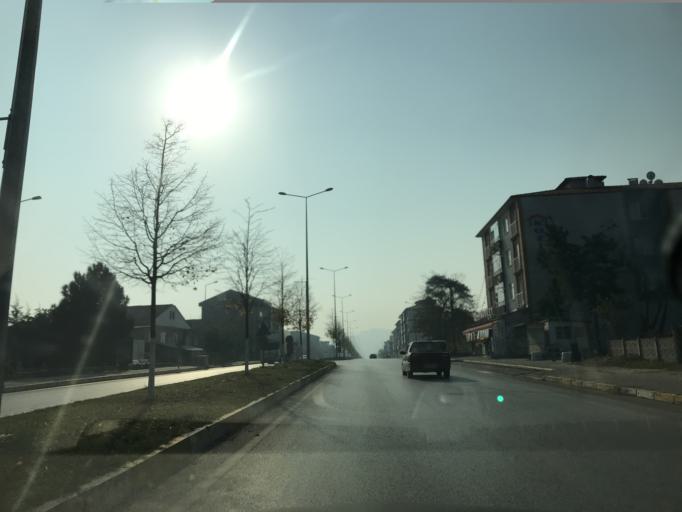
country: TR
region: Duzce
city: Cumayeri
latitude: 40.8711
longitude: 30.9513
